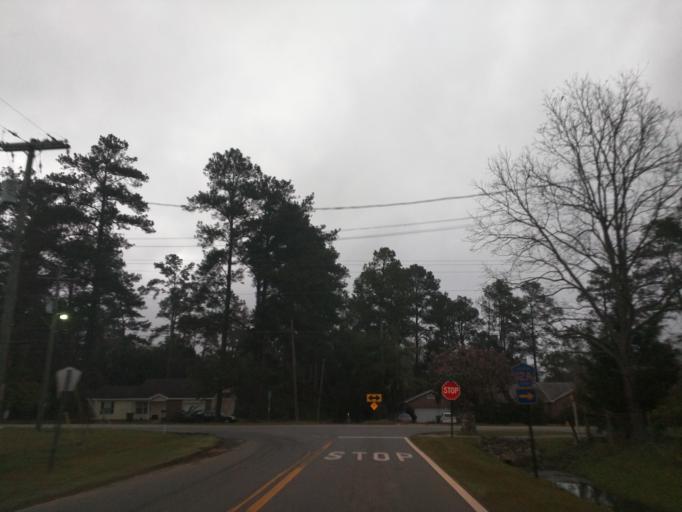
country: US
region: Florida
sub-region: Gadsden County
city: Havana
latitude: 30.6237
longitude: -84.4048
